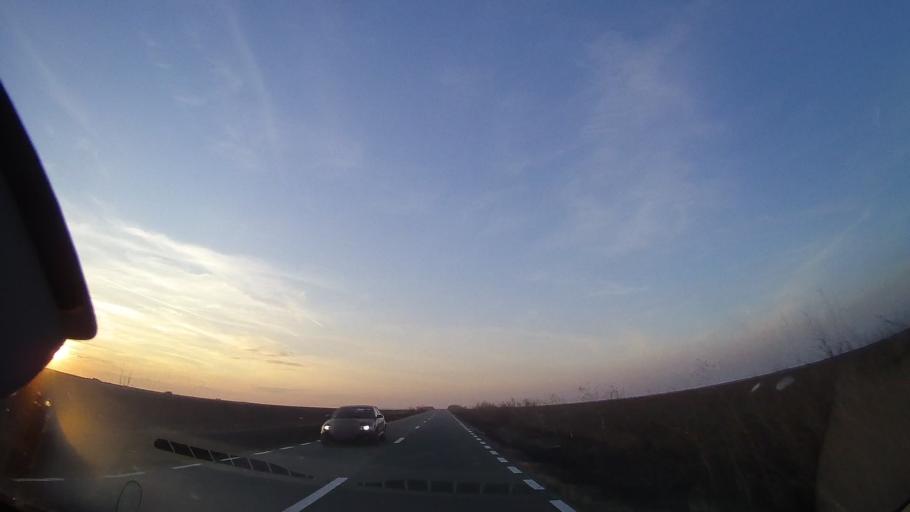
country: RO
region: Constanta
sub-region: Comuna Topraisar
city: Topraisar
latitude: 44.0222
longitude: 28.4124
